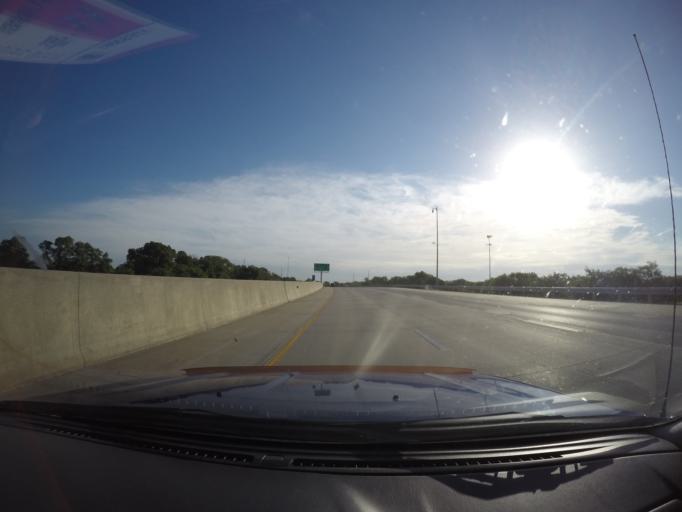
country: US
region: Kansas
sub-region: Wyandotte County
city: Kansas City
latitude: 39.1418
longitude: -94.6720
